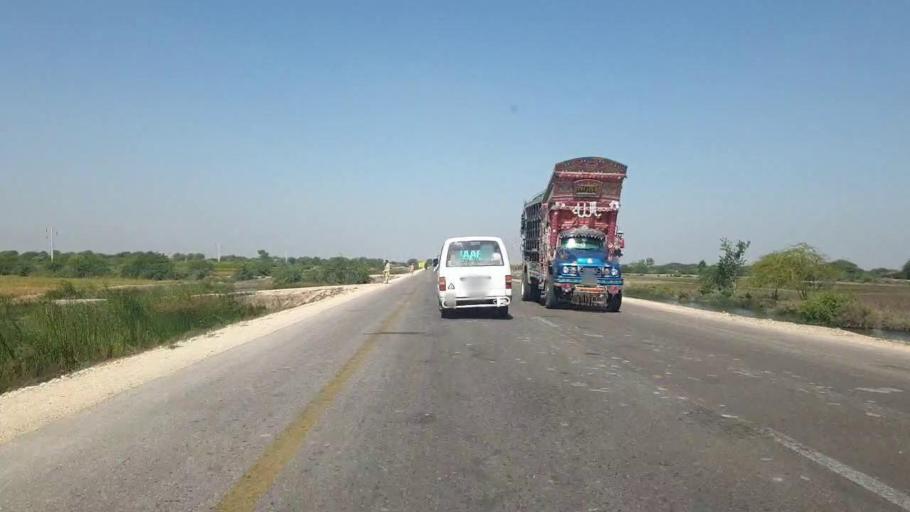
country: PK
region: Sindh
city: Talhar
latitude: 24.8255
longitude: 68.8159
